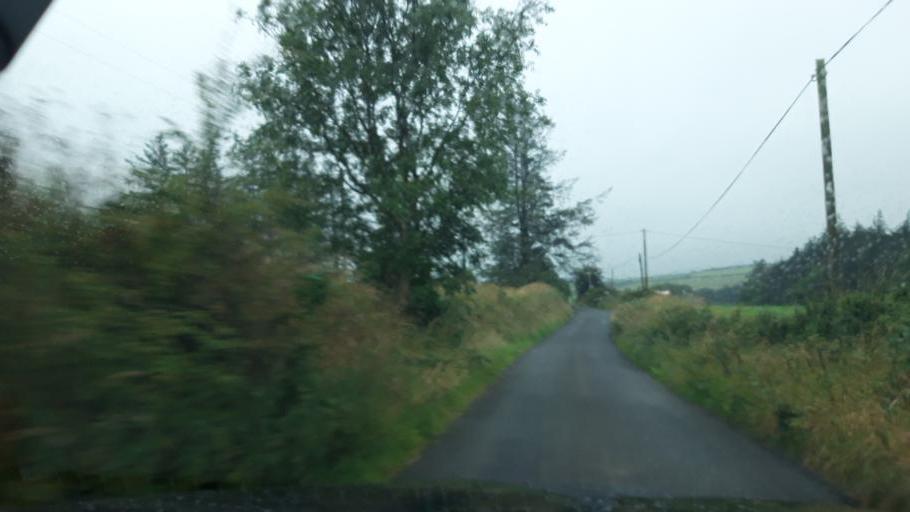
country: IE
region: Leinster
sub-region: Kilkenny
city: Callan
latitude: 52.6318
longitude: -7.5456
